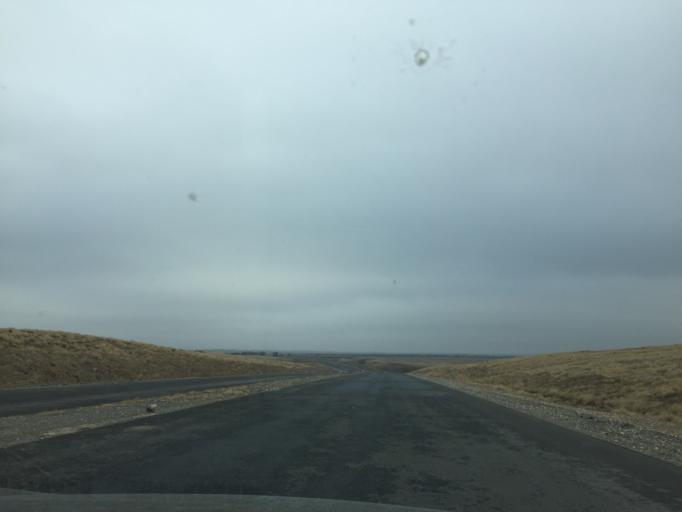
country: KZ
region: Ongtustik Qazaqstan
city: Kokterek
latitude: 42.5437
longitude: 70.1875
